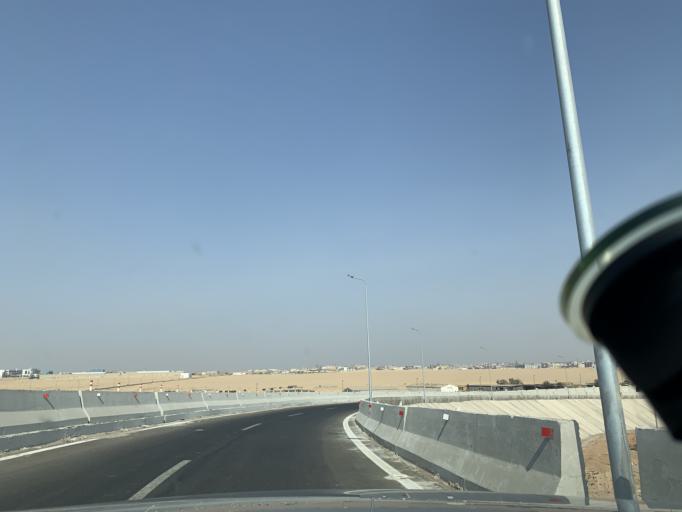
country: EG
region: Muhafazat al Qalyubiyah
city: Al Khankah
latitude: 30.2015
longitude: 31.4184
